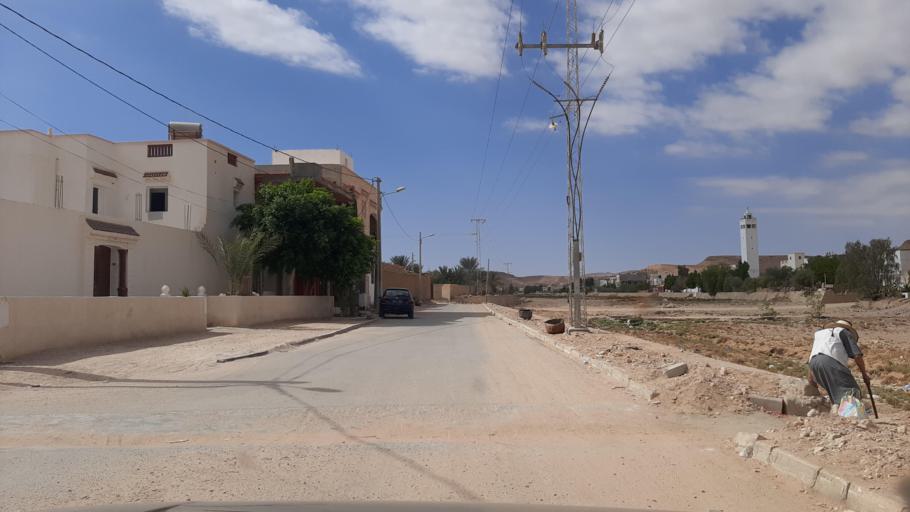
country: TN
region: Tataouine
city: Tataouine
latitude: 32.9317
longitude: 10.4454
